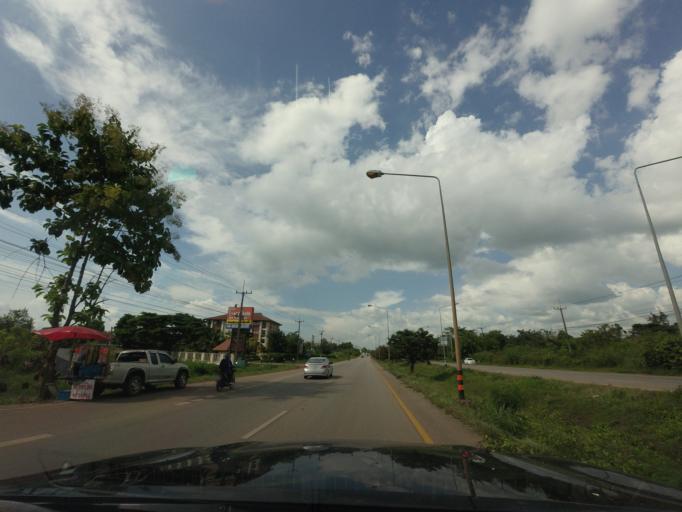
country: TH
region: Nong Khai
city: Sa Khrai
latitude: 17.5618
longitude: 102.8013
